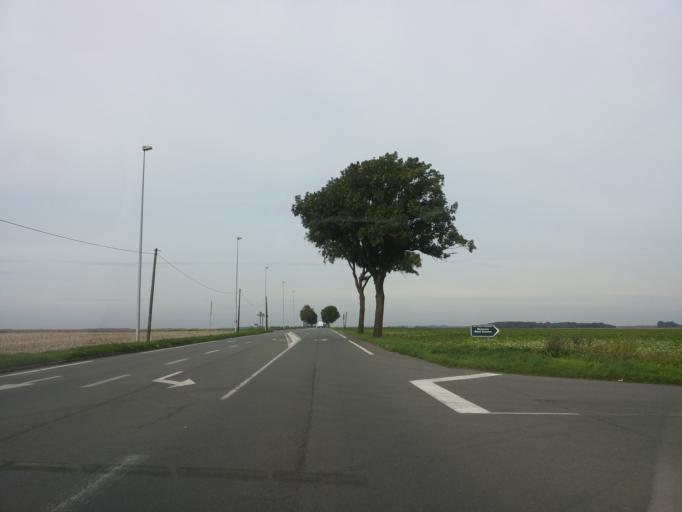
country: FR
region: Nord-Pas-de-Calais
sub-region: Departement du Pas-de-Calais
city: Bourlon
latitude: 50.1980
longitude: 3.1376
